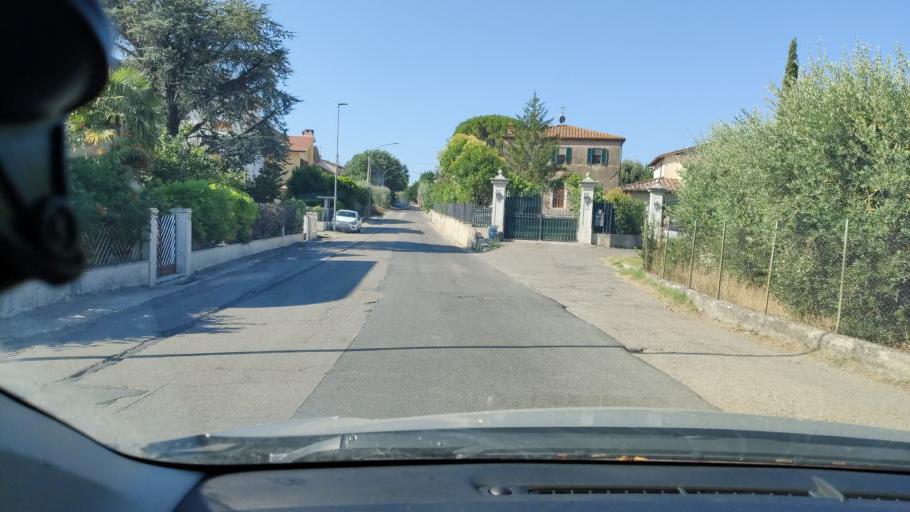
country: IT
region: Umbria
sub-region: Provincia di Terni
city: Fornole
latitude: 42.5420
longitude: 12.4550
